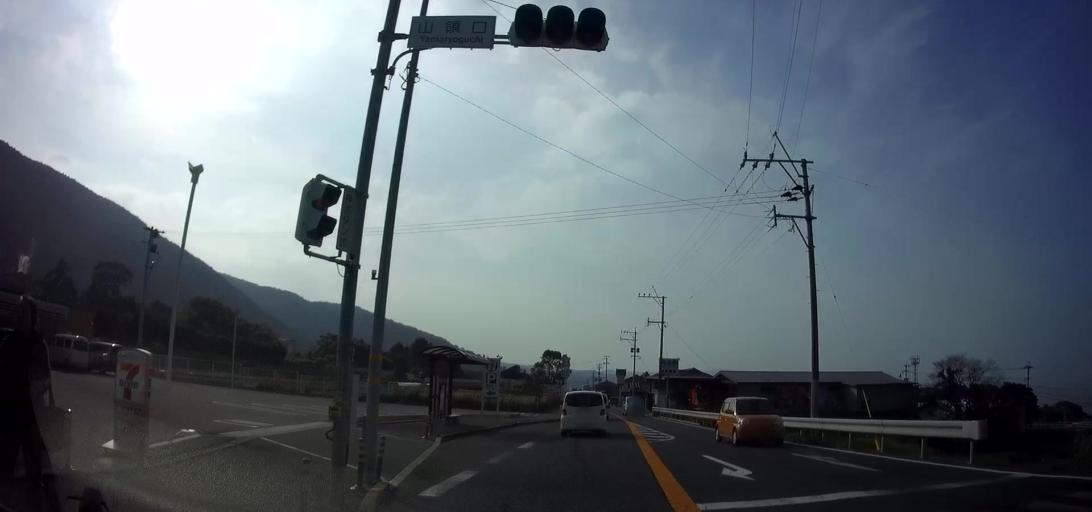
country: JP
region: Nagasaki
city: Shimabara
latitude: 32.7511
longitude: 130.2111
